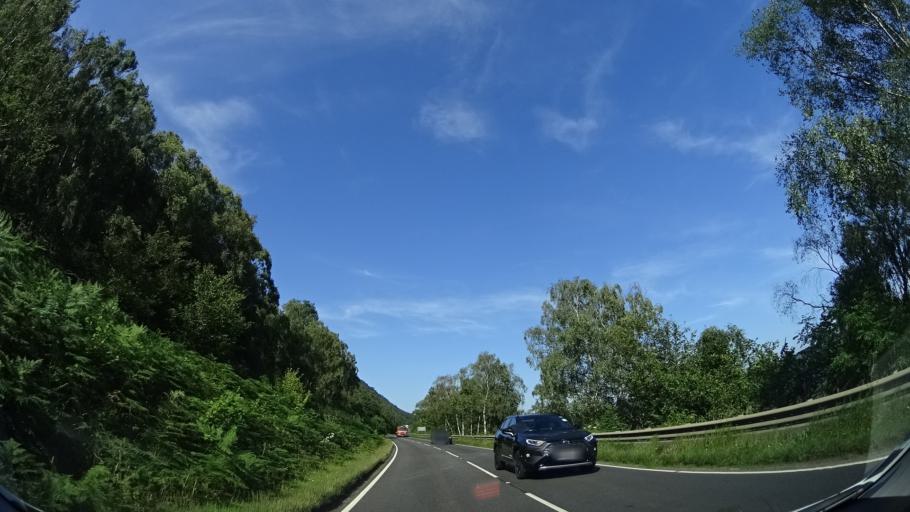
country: GB
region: Scotland
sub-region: Highland
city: Beauly
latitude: 57.3848
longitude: -4.3719
